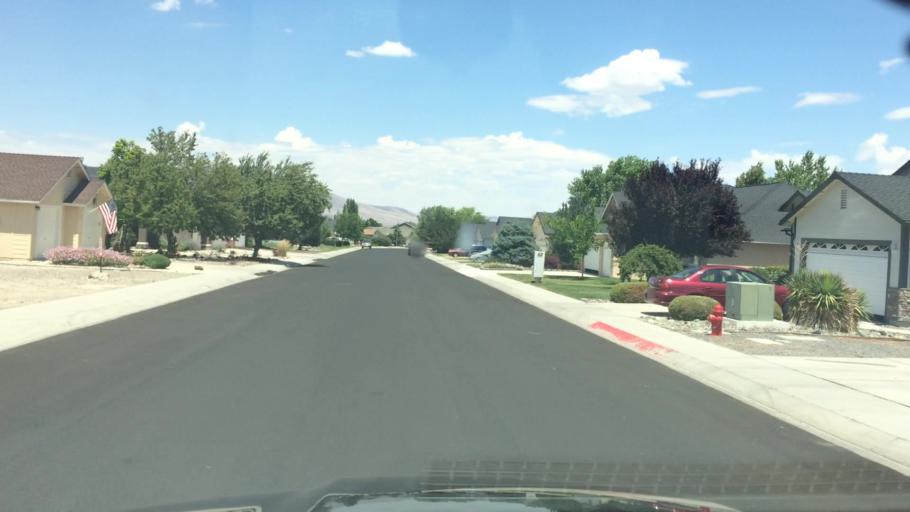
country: US
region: Nevada
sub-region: Lyon County
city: Fernley
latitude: 39.5853
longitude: -119.1411
